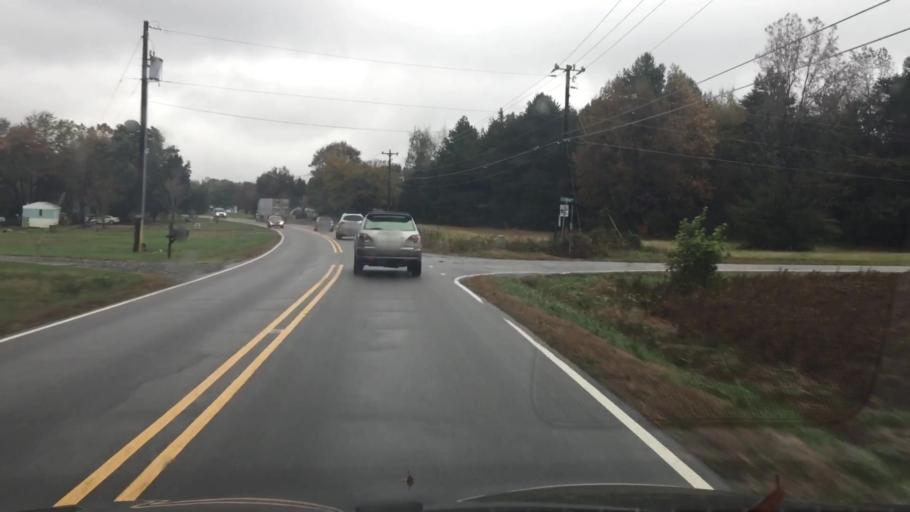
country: US
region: North Carolina
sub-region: Iredell County
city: Mooresville
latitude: 35.6019
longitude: -80.7559
